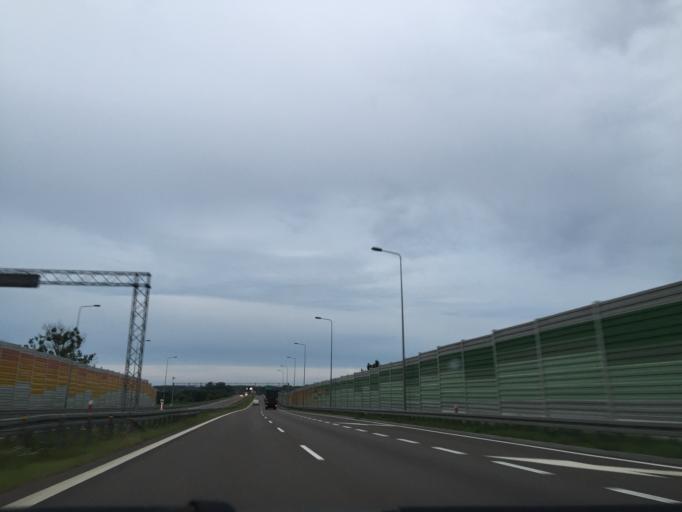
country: PL
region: Podlasie
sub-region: Powiat bialostocki
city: Choroszcz
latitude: 53.1642
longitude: 22.9508
